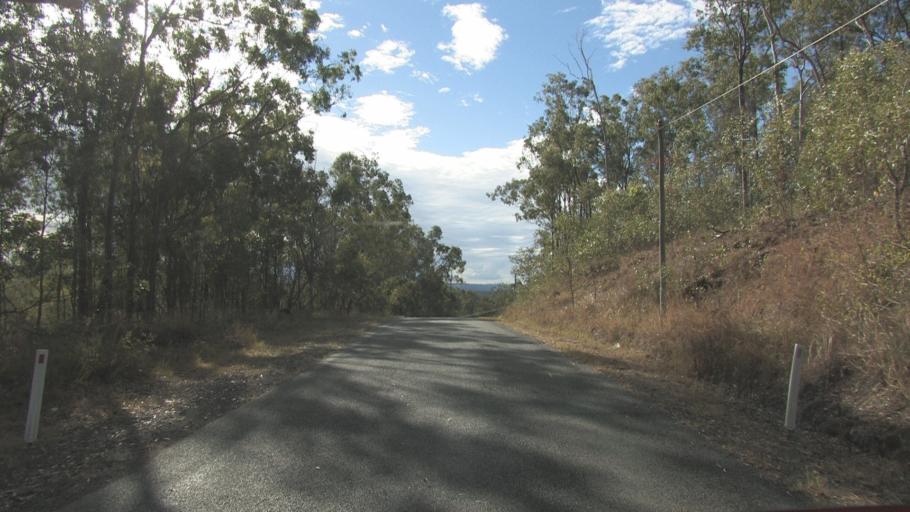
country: AU
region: Queensland
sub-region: Logan
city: Cedar Vale
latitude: -27.8481
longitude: 153.0733
